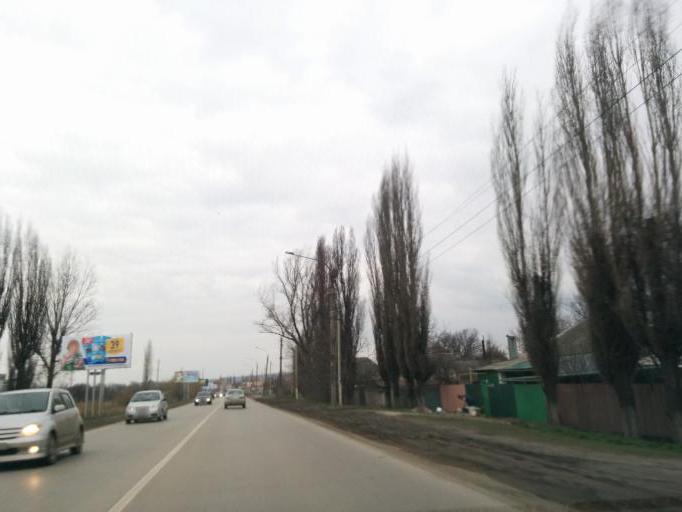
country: RU
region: Rostov
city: Novocherkassk
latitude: 47.4609
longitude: 40.1007
